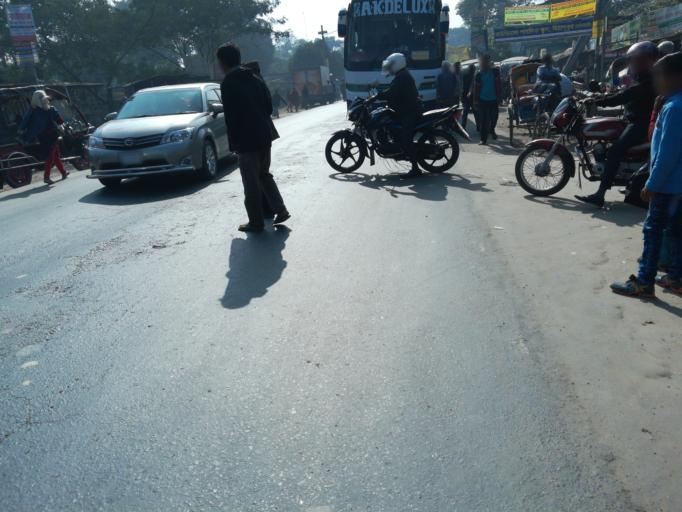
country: BD
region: Rangpur Division
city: Rangpur
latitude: 25.5708
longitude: 89.2743
